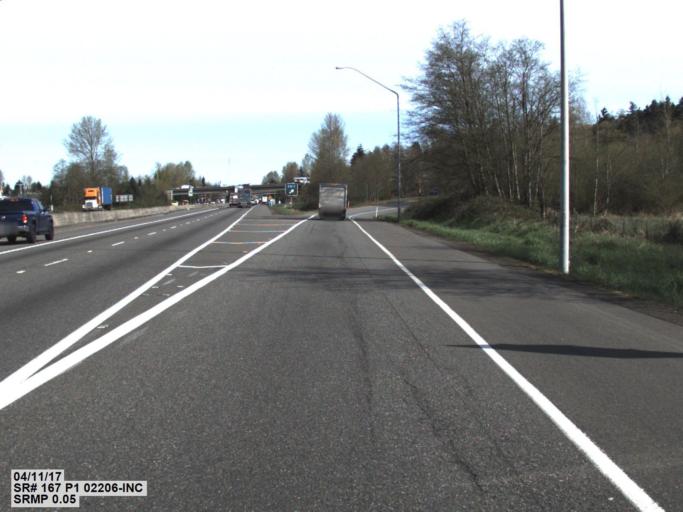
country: US
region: Washington
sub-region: Pierce County
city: Tacoma
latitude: 47.2387
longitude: -122.4067
